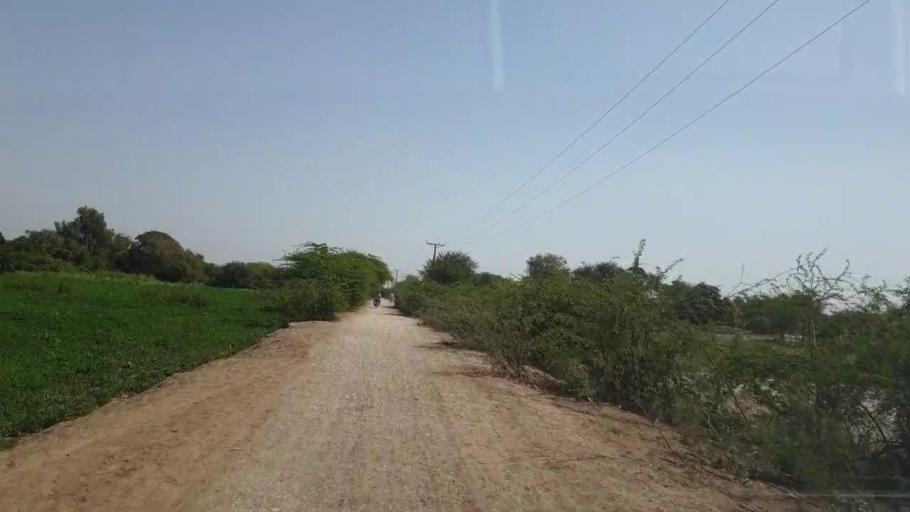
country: PK
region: Sindh
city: Naukot
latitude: 24.9745
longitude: 69.4902
